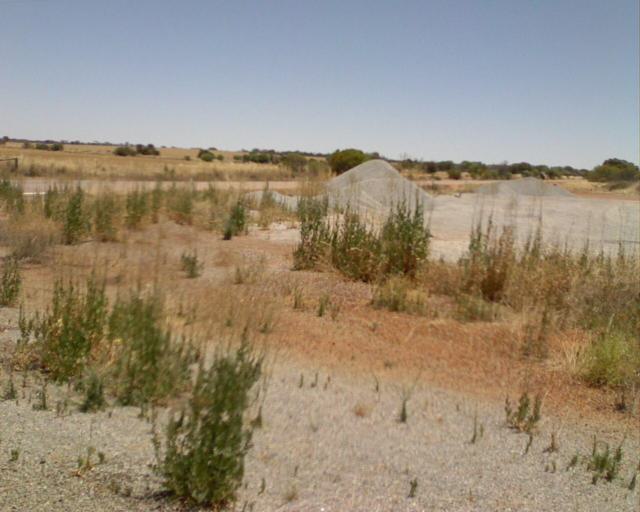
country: AU
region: Western Australia
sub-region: Merredin
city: Merredin
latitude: -30.8327
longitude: 117.8624
